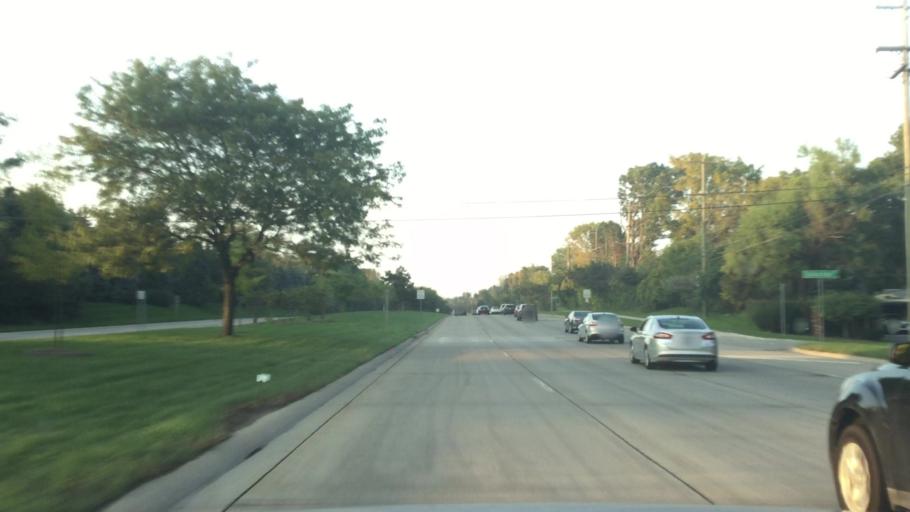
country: US
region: Michigan
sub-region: Oakland County
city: Bloomfield Hills
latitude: 42.5873
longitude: -83.2812
